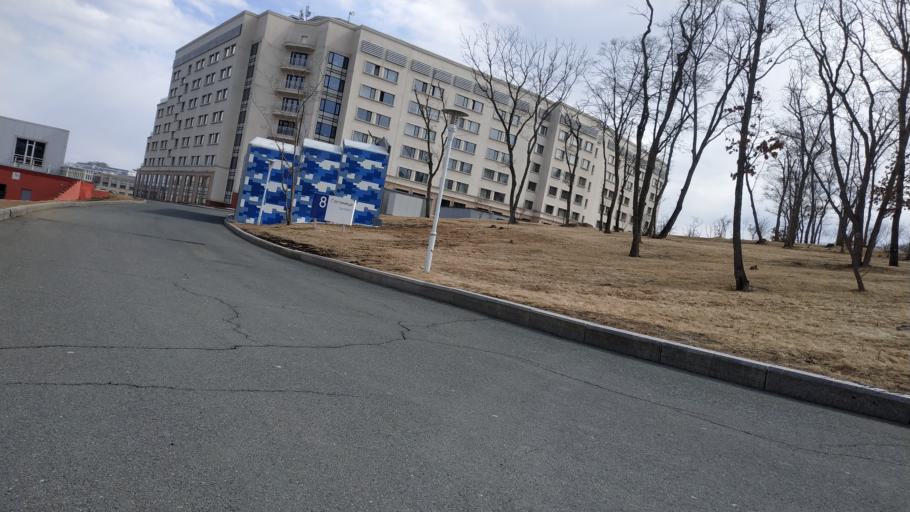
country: RU
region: Primorskiy
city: Russkiy
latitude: 43.0296
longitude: 131.8854
